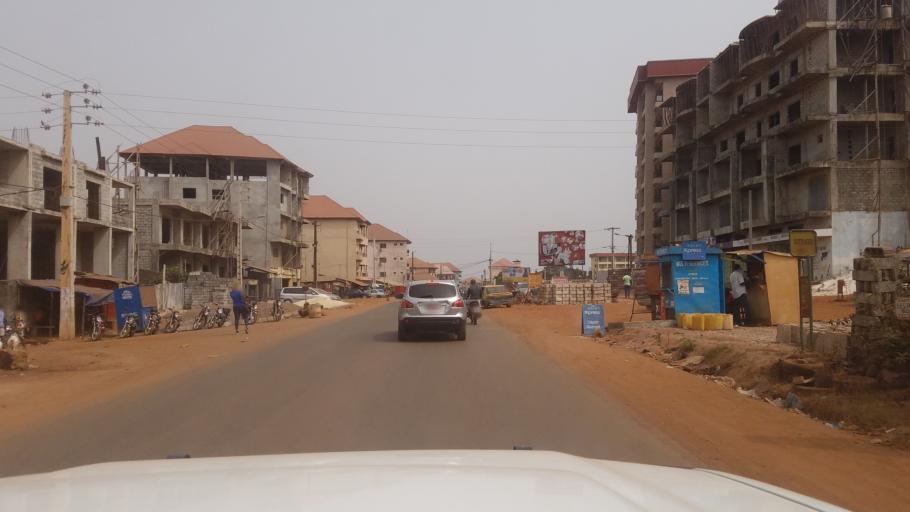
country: GN
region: Conakry
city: Conakry
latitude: 9.6570
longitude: -13.5998
